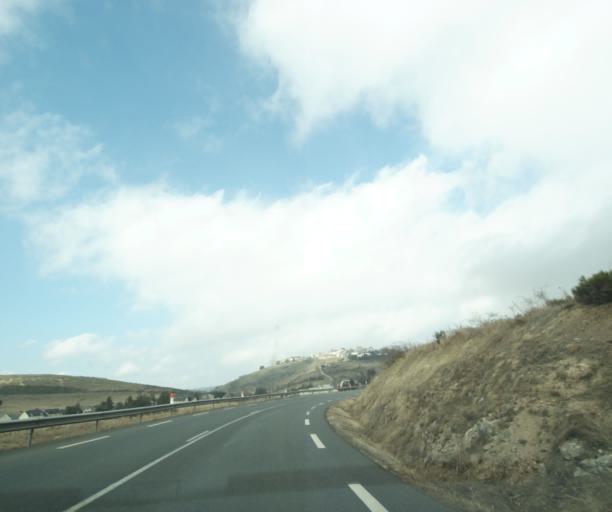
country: FR
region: Languedoc-Roussillon
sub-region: Departement de la Lozere
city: Langogne
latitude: 44.6281
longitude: 3.6750
